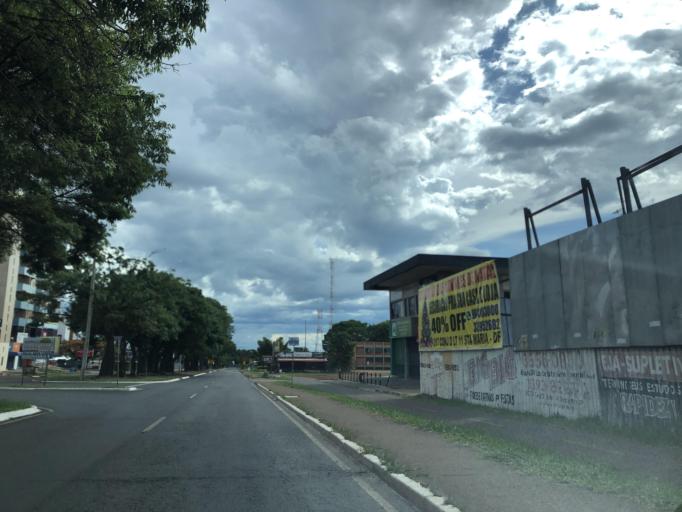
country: BR
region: Goias
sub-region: Luziania
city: Luziania
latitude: -16.0174
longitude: -48.0666
